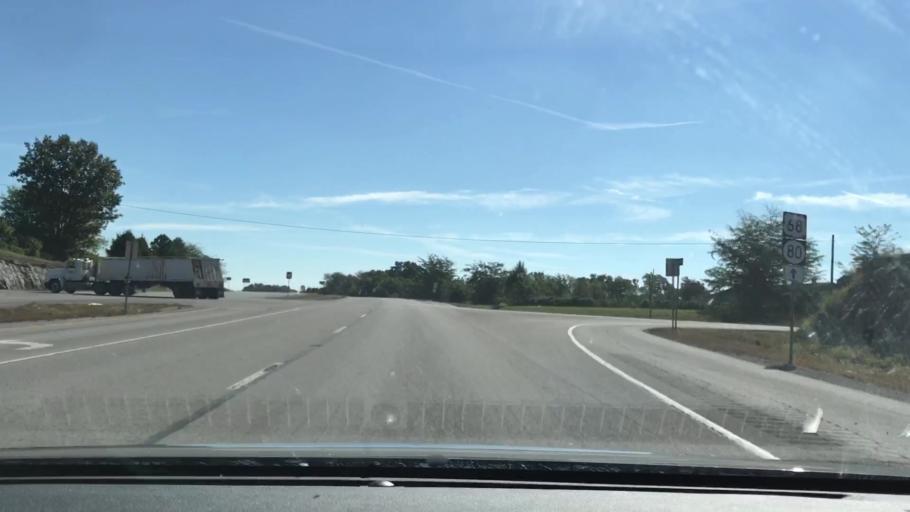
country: US
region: Kentucky
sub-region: Todd County
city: Elkton
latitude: 36.8272
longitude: -87.2214
